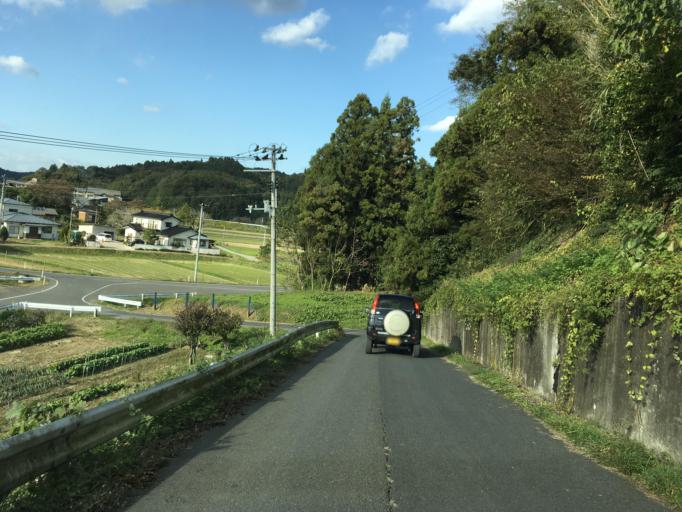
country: JP
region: Miyagi
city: Wakuya
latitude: 38.6510
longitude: 141.2914
